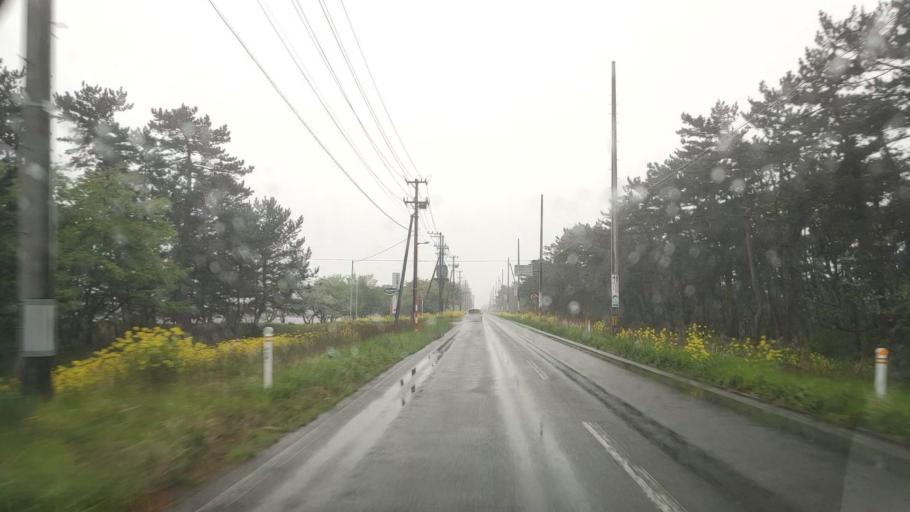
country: JP
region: Akita
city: Tenno
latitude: 40.0059
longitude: 139.9492
